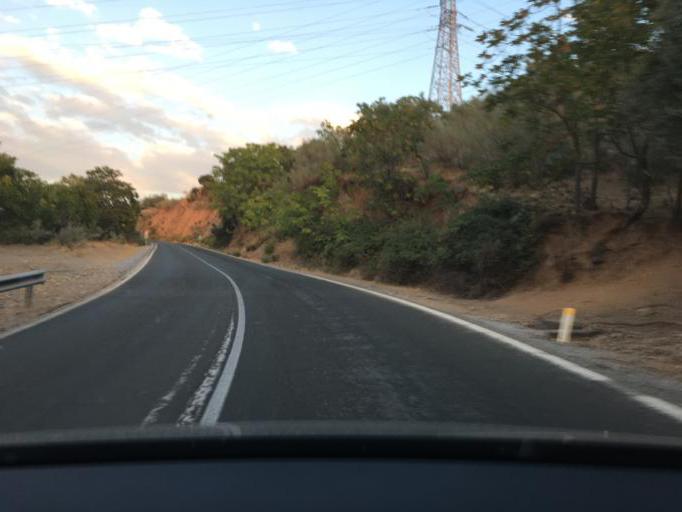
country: ES
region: Andalusia
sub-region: Provincia de Granada
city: Jun
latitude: 37.1979
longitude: -3.5758
